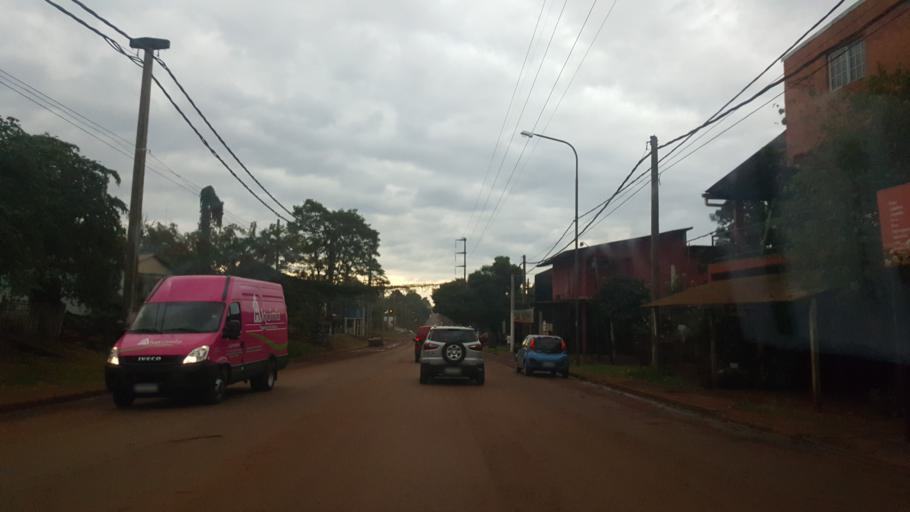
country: AR
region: Misiones
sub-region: Departamento de Capital
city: Posadas
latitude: -27.4239
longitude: -55.9137
